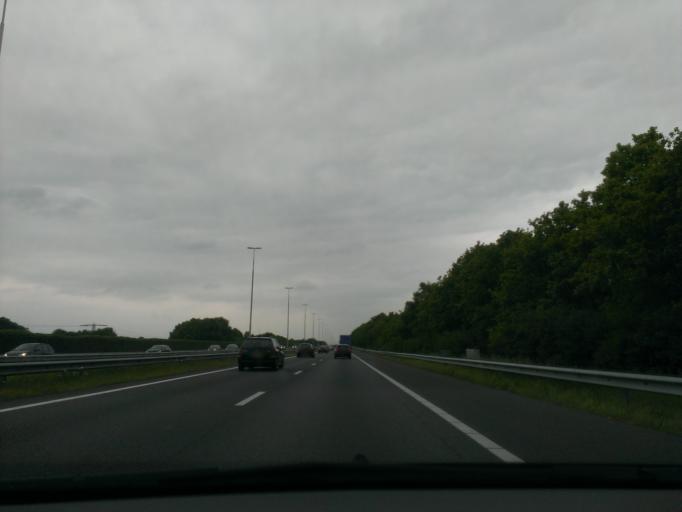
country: NL
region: Gelderland
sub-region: Gemeente Apeldoorn
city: Apeldoorn
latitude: 52.2244
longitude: 6.0194
